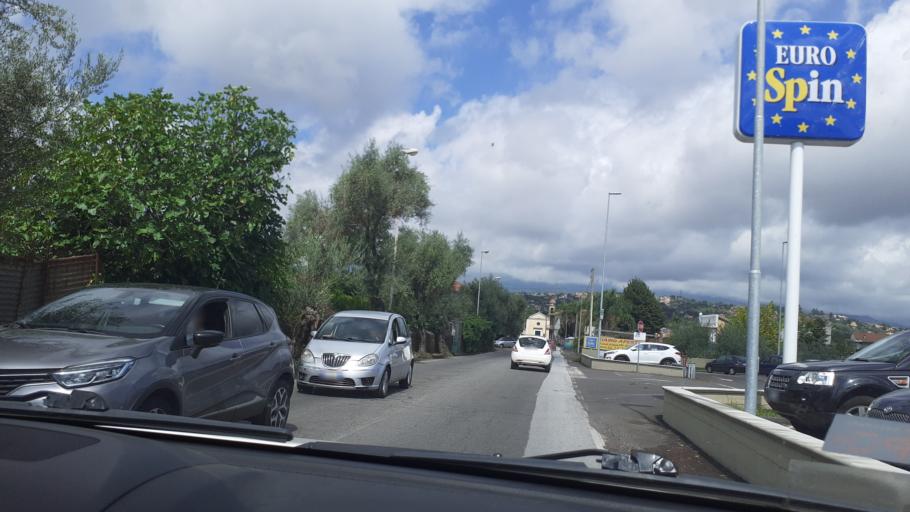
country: IT
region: Sicily
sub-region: Catania
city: San Giovanni la Punta
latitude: 37.5867
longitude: 15.0896
